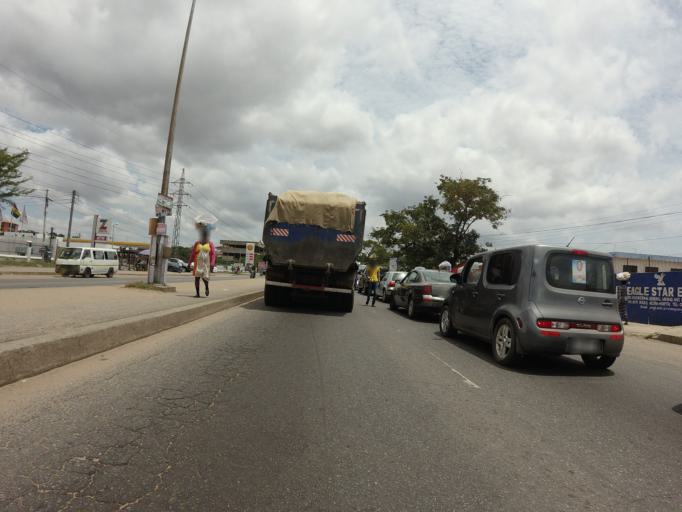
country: GH
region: Greater Accra
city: Gbawe
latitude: 5.5747
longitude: -0.2771
